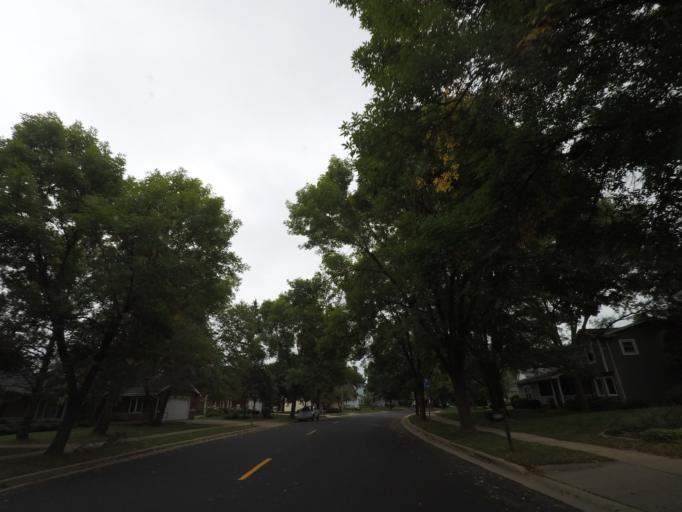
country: US
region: Wisconsin
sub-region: Dane County
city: Middleton
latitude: 43.0811
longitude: -89.5067
